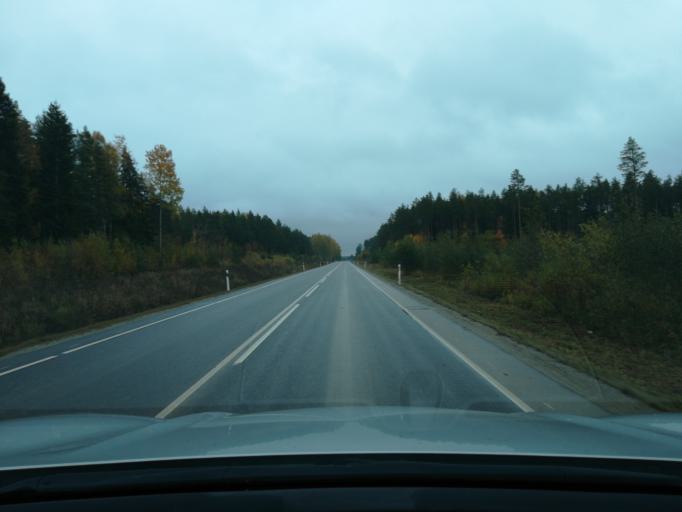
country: EE
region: Ida-Virumaa
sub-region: Johvi vald
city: Johvi
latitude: 59.2994
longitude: 27.4746
